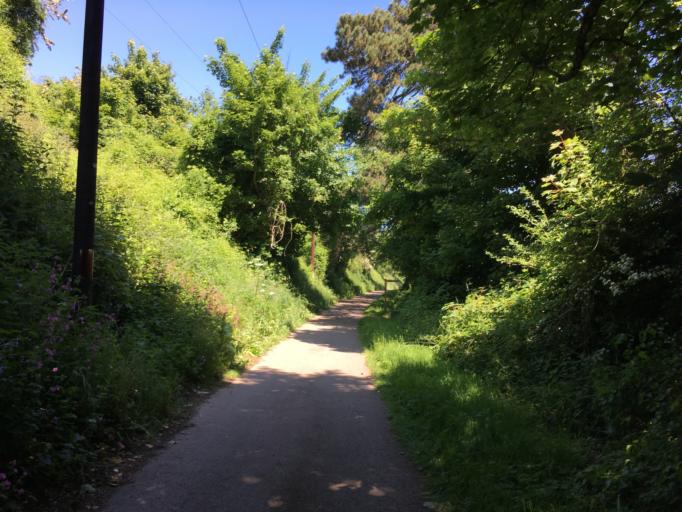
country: GB
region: England
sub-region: Devon
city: Dartmouth
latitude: 50.3433
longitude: -3.5583
